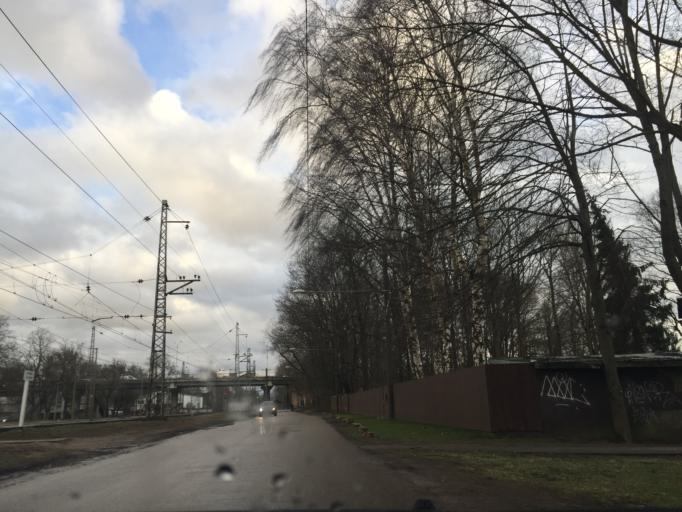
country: LV
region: Marupe
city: Marupe
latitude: 56.9411
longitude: 24.0511
